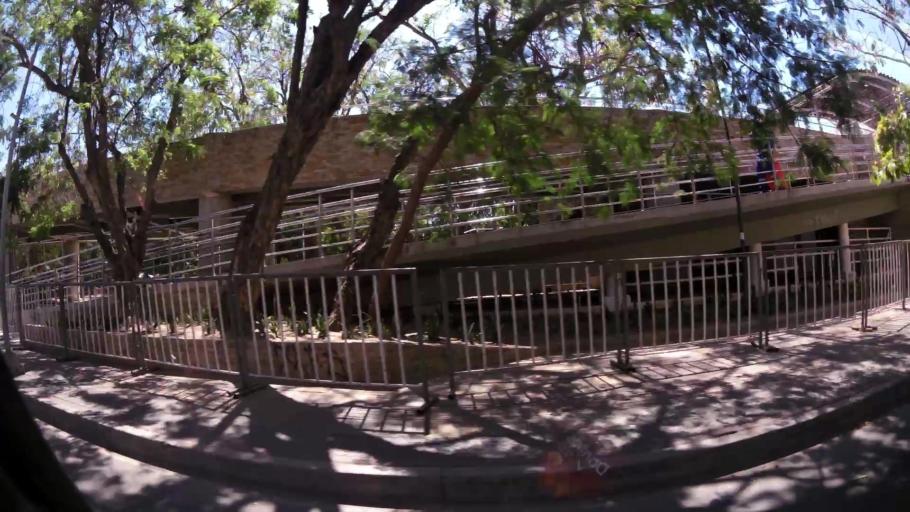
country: CO
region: Atlantico
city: Barranquilla
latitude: 10.9882
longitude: -74.7883
